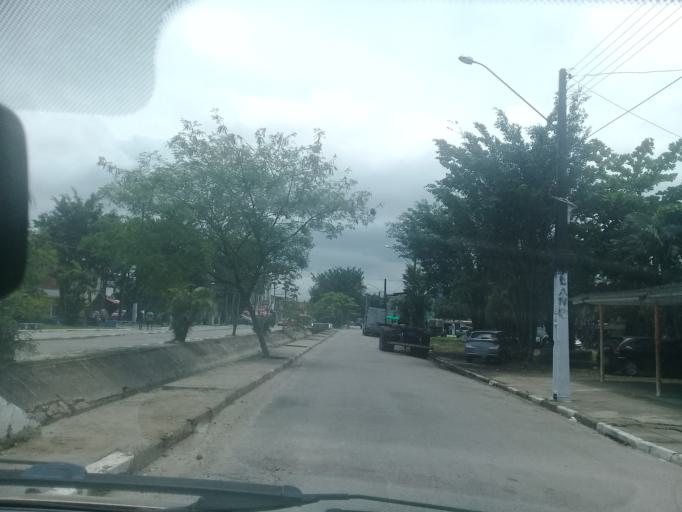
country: BR
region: Sao Paulo
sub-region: Guaruja
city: Guaruja
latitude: -23.9650
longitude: -46.2542
